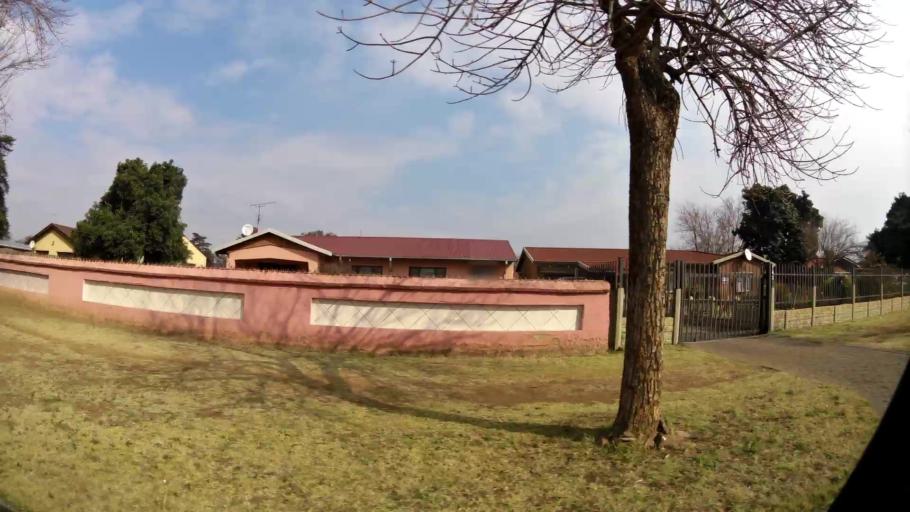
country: ZA
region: Gauteng
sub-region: Sedibeng District Municipality
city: Vanderbijlpark
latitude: -26.6913
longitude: 27.8468
